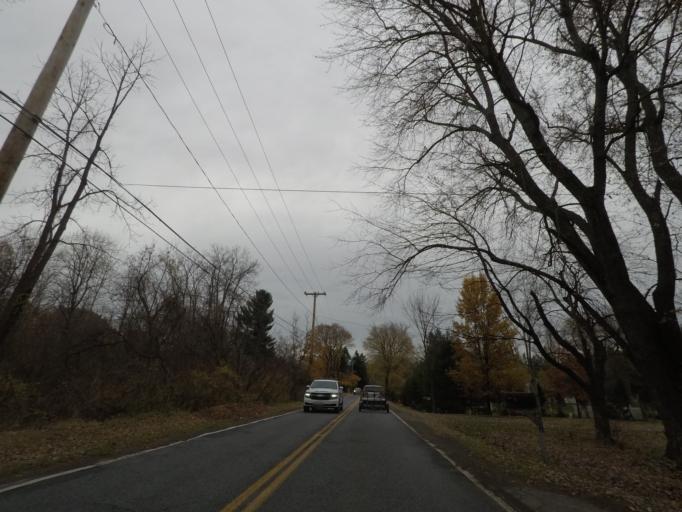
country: US
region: New York
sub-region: Rensselaer County
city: Wynantskill
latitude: 42.7285
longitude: -73.6564
